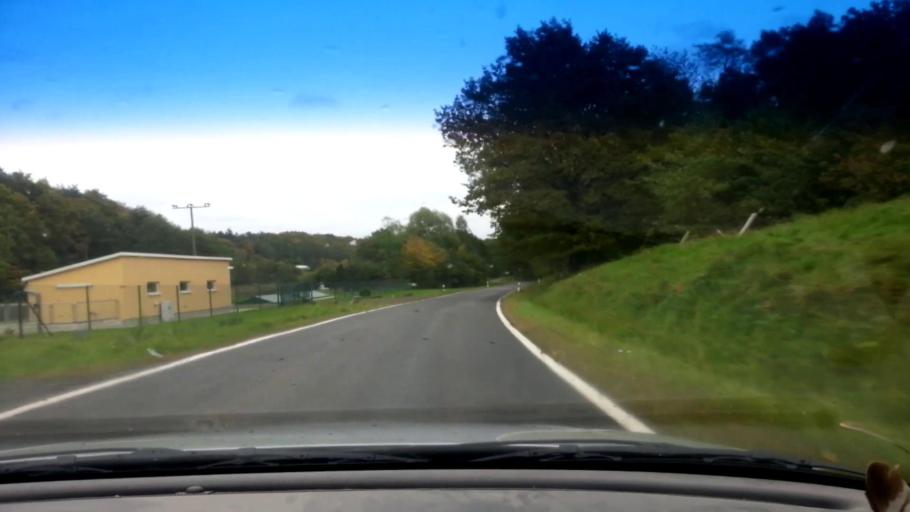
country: DE
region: Bavaria
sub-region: Regierungsbezirk Unterfranken
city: Kirchlauter
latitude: 50.0376
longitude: 10.7254
